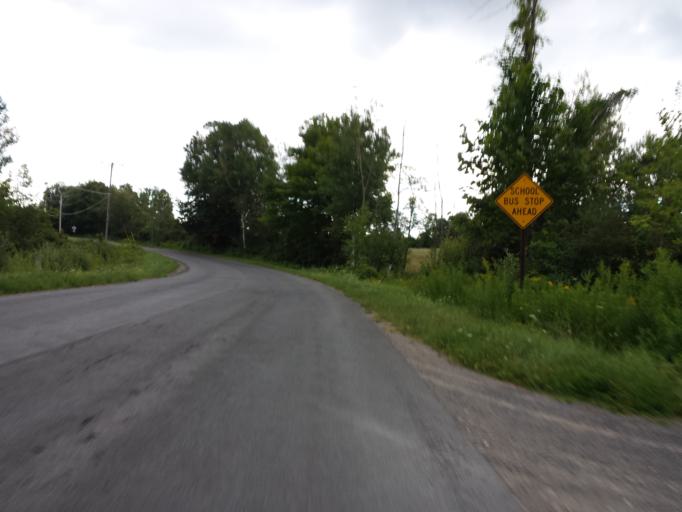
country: US
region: New York
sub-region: St. Lawrence County
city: Potsdam
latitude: 44.6858
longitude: -75.0104
